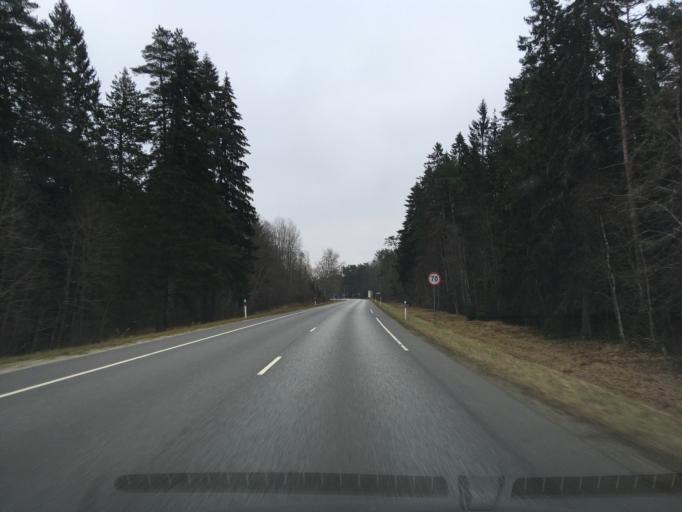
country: EE
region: Laeaene-Virumaa
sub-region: Kadrina vald
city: Kadrina
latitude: 59.4574
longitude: 26.0018
